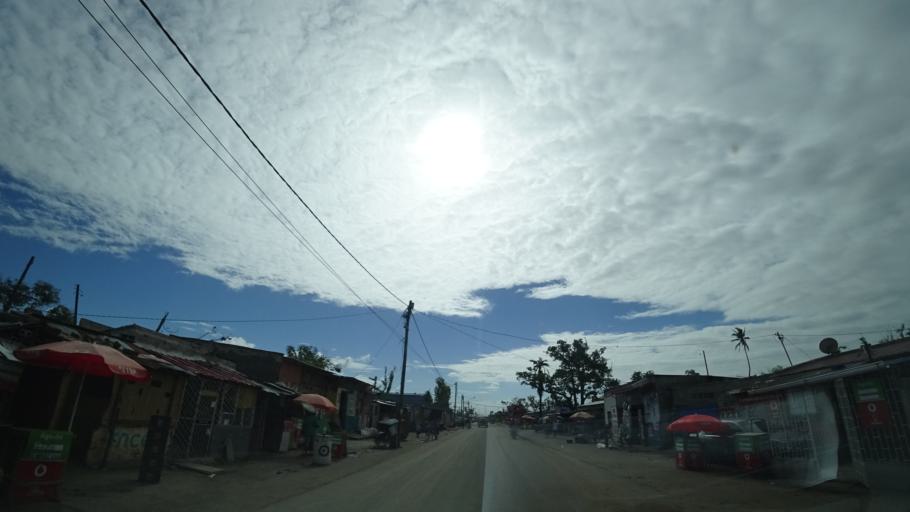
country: MZ
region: Sofala
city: Beira
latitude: -19.7899
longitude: 34.8861
